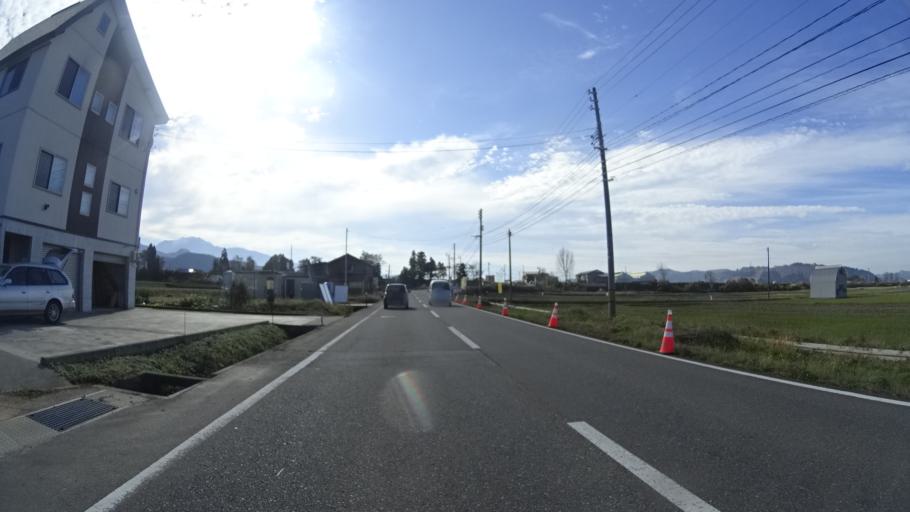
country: JP
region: Niigata
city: Ojiya
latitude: 37.2403
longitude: 138.9798
